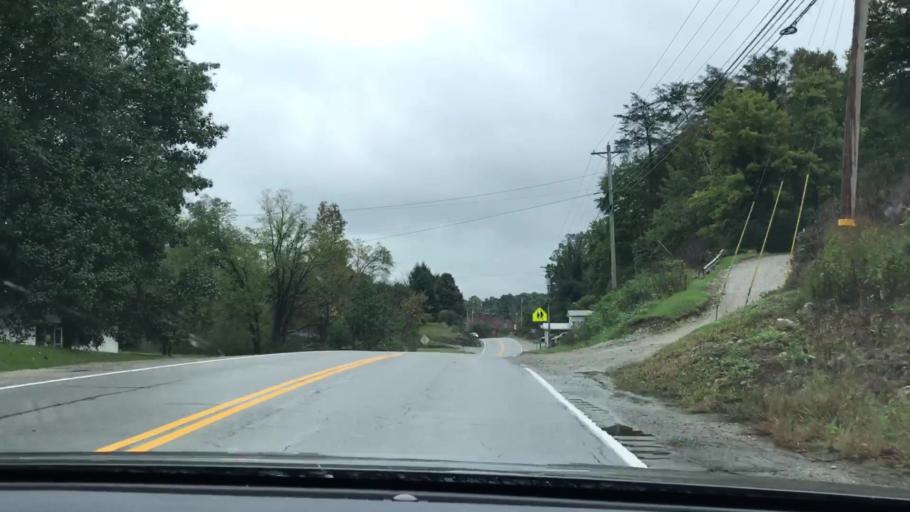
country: US
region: Tennessee
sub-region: Scott County
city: Huntsville
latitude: 36.3485
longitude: -84.5891
